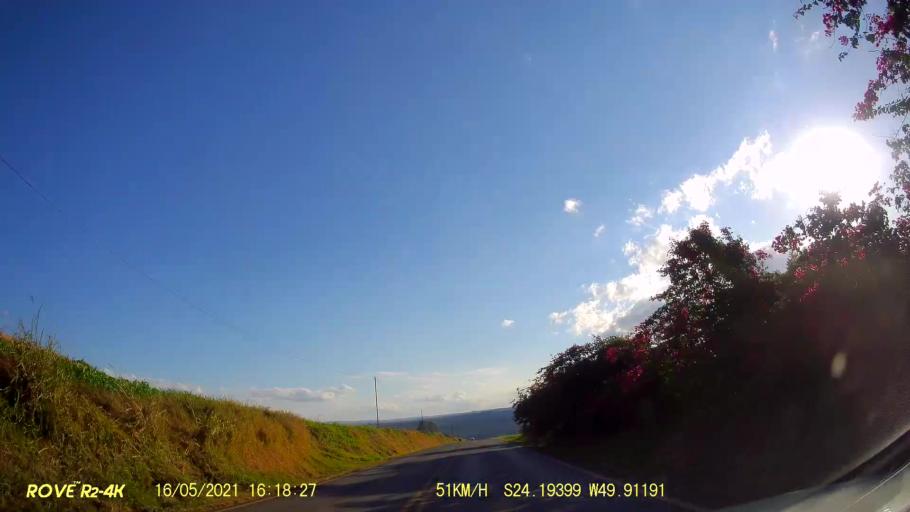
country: BR
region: Parana
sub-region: Jaguariaiva
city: Jaguariaiva
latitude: -24.1940
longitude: -49.9121
